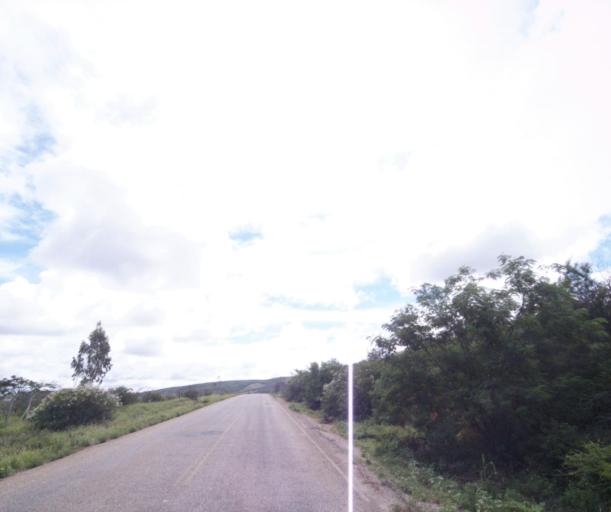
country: BR
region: Bahia
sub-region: Brumado
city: Brumado
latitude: -14.1990
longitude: -41.5972
